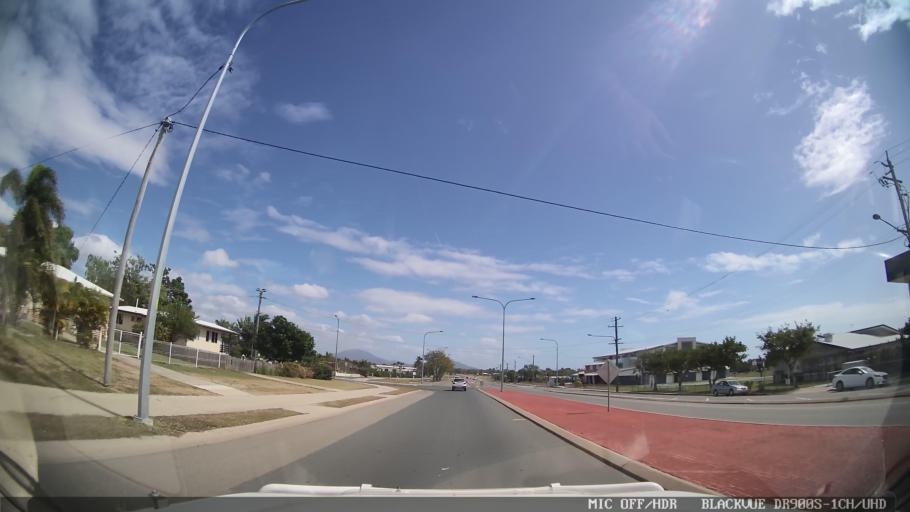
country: AU
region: Queensland
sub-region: Whitsunday
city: Bowen
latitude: -20.0003
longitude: 148.2342
